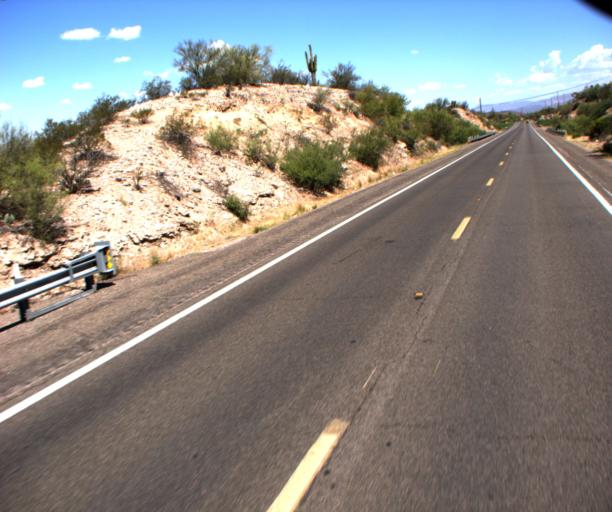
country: US
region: Arizona
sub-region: Pinal County
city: Mammoth
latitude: 32.9220
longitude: -110.7256
